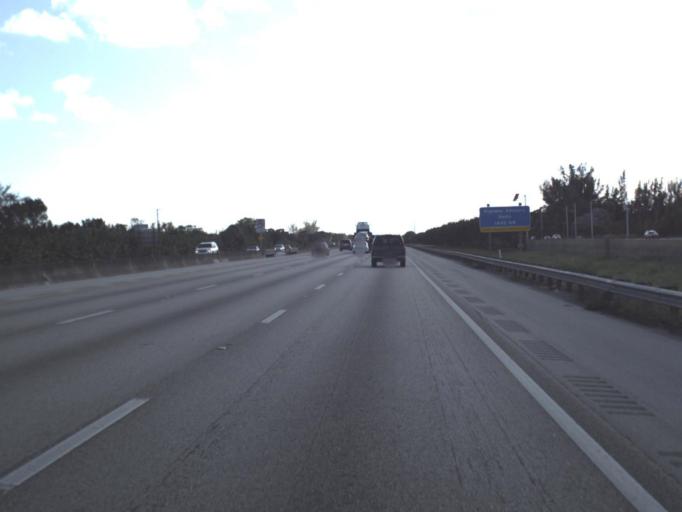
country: US
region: Florida
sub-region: Palm Beach County
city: Boca Del Mar
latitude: 26.3608
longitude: -80.1708
